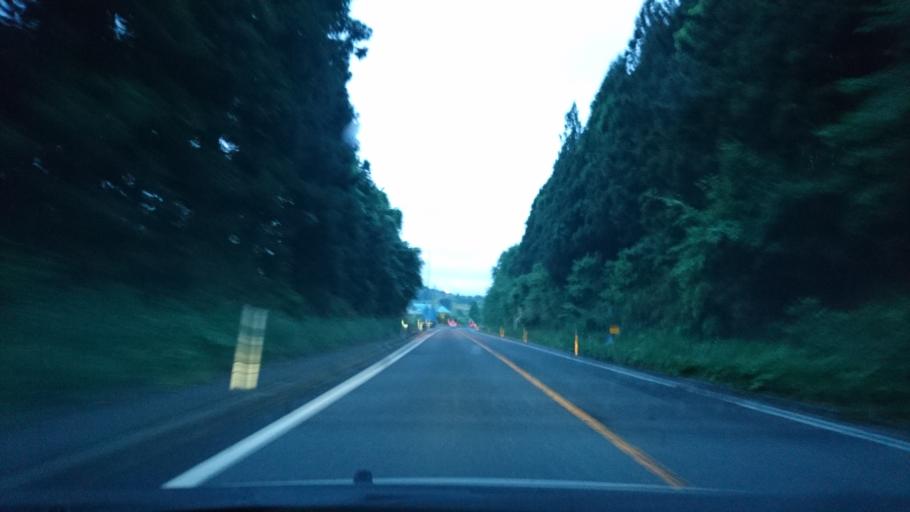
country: JP
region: Iwate
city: Ichinoseki
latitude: 38.8553
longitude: 141.0981
